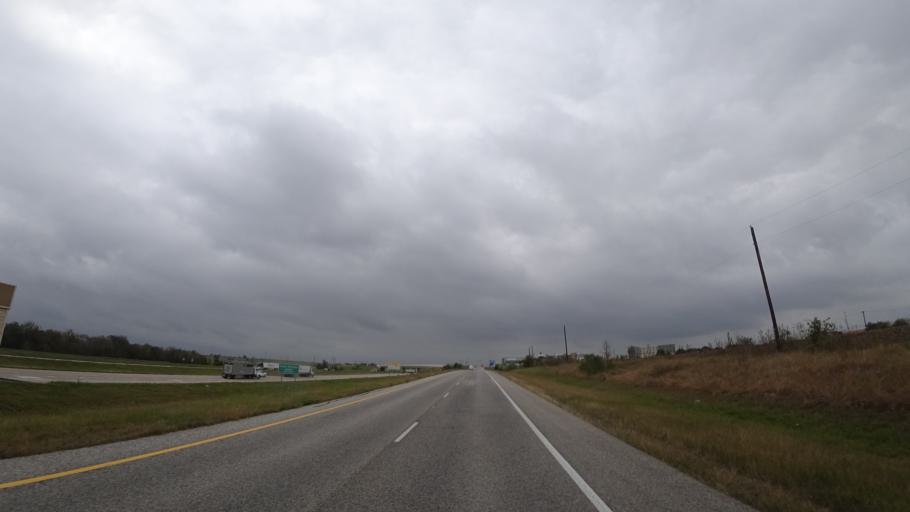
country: US
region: Texas
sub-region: Travis County
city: Pflugerville
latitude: 30.4276
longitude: -97.5899
